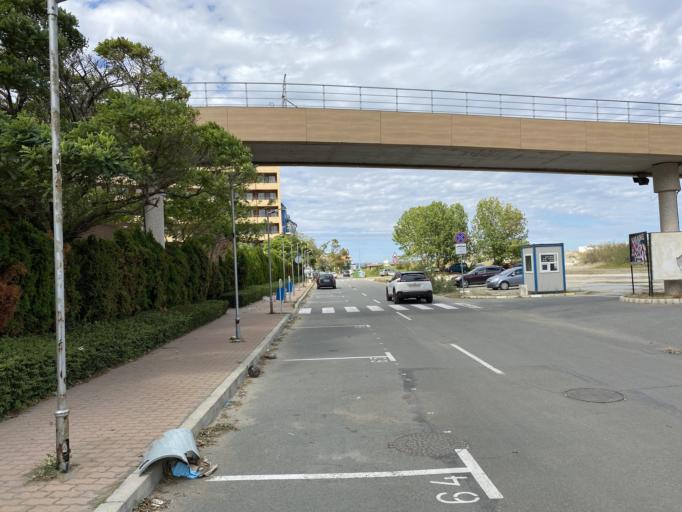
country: BG
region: Burgas
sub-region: Obshtina Pomorie
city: Pomorie
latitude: 42.5660
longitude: 27.6384
